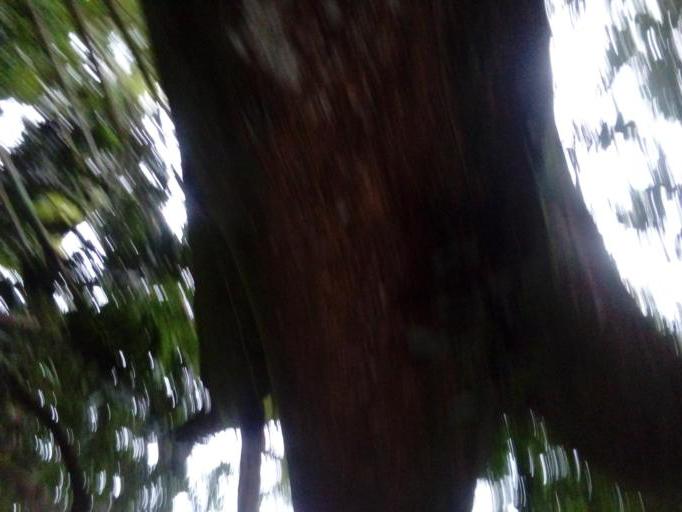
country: CR
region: Alajuela
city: Pocosol
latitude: 10.3307
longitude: -84.5842
